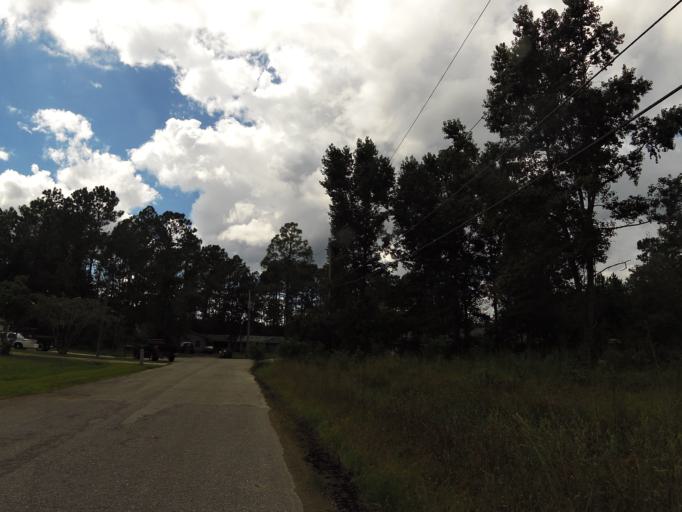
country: US
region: Florida
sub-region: Saint Johns County
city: Saint Augustine
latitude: 29.9204
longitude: -81.4996
